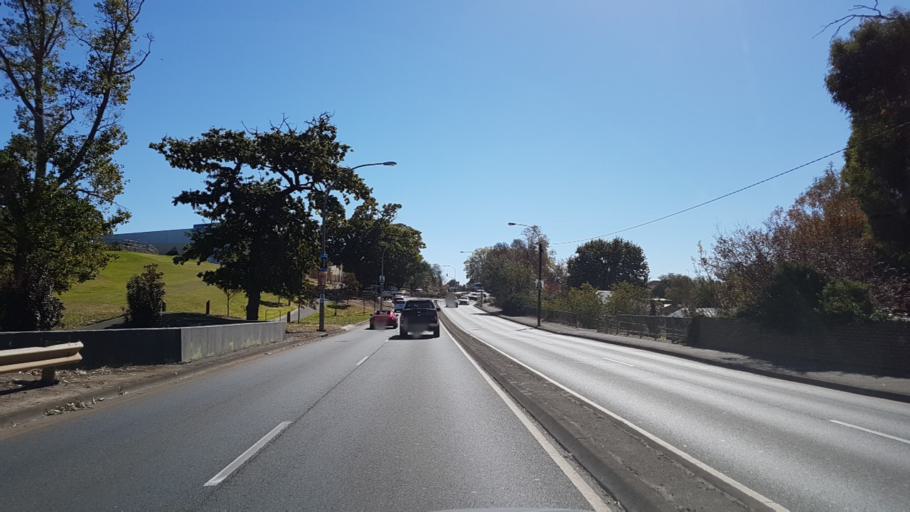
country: AU
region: South Australia
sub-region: Mount Barker
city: Mount Barker
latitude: -35.0705
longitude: 138.8572
